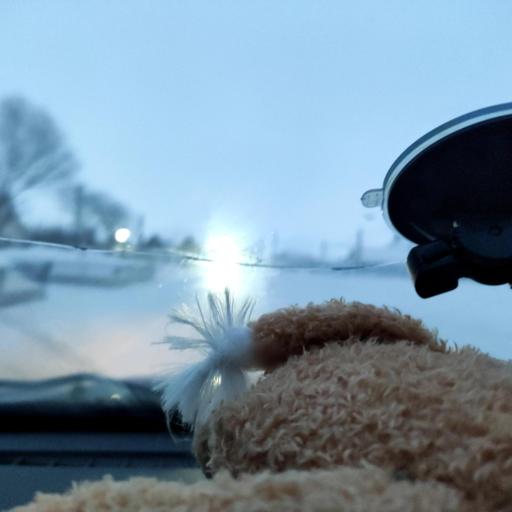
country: RU
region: Samara
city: Podstepki
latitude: 53.5100
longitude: 49.1757
